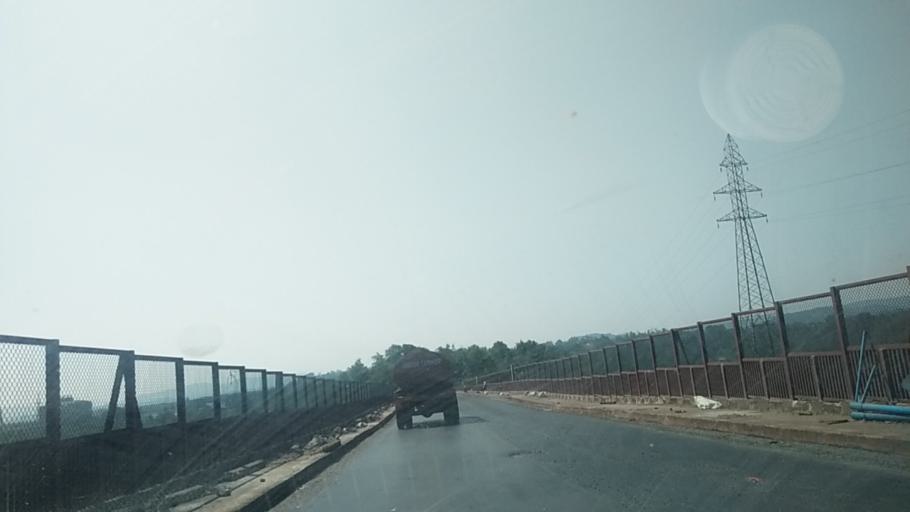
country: IN
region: Goa
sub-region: North Goa
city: Queula
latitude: 15.3488
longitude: 74.0026
